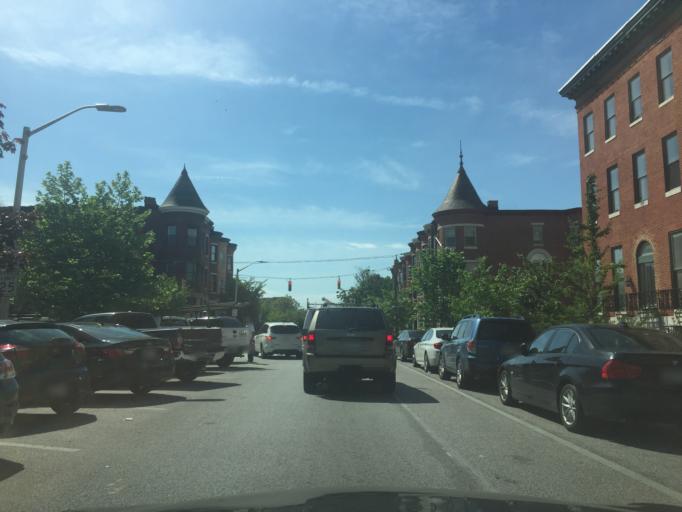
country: US
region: Maryland
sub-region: City of Baltimore
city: Baltimore
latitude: 39.3129
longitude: -76.6381
